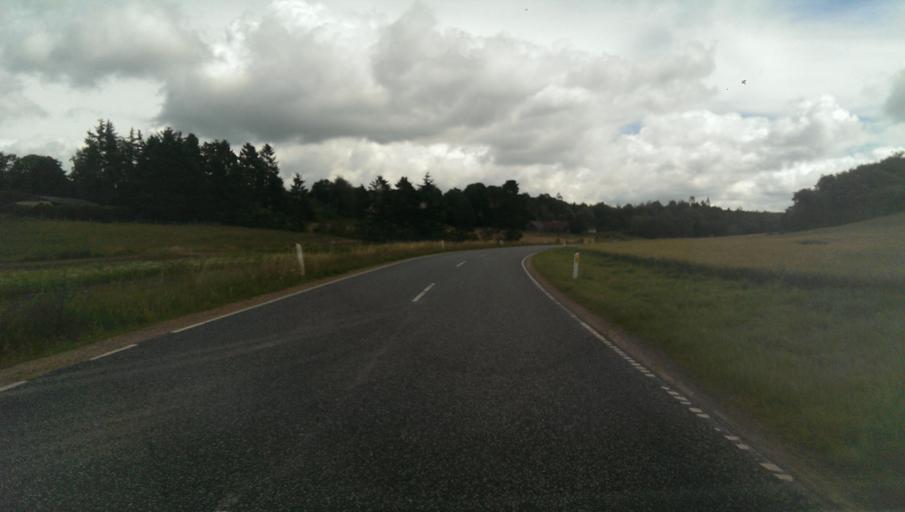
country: DK
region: Central Jutland
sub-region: Silkeborg Kommune
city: Svejbaek
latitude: 56.0987
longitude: 9.6333
